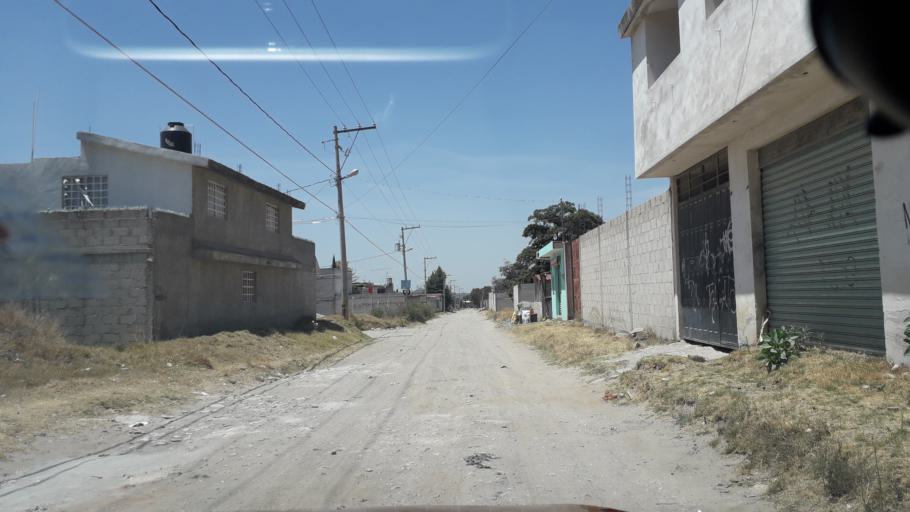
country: MX
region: Puebla
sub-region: Amozoc
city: Casa Blanca
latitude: 19.0566
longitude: -98.1184
